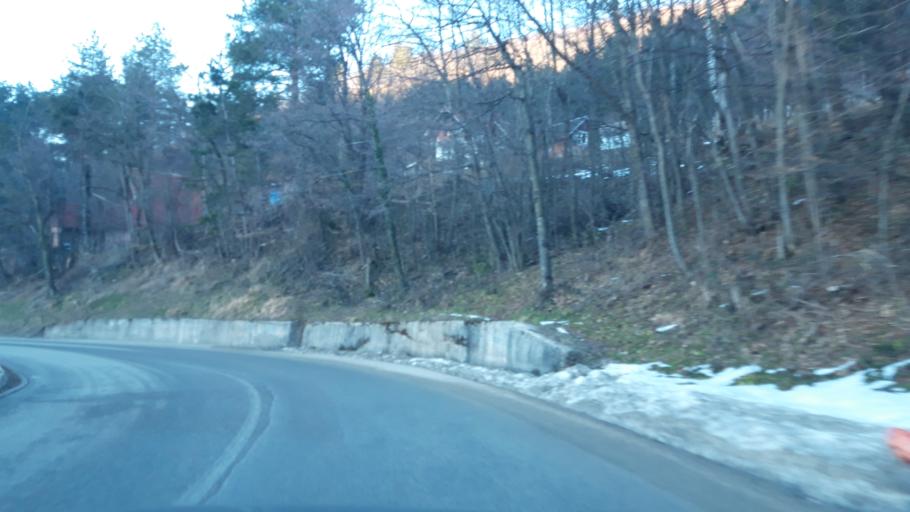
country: BA
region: Republika Srpska
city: Vlasenica
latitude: 44.1668
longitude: 18.9515
